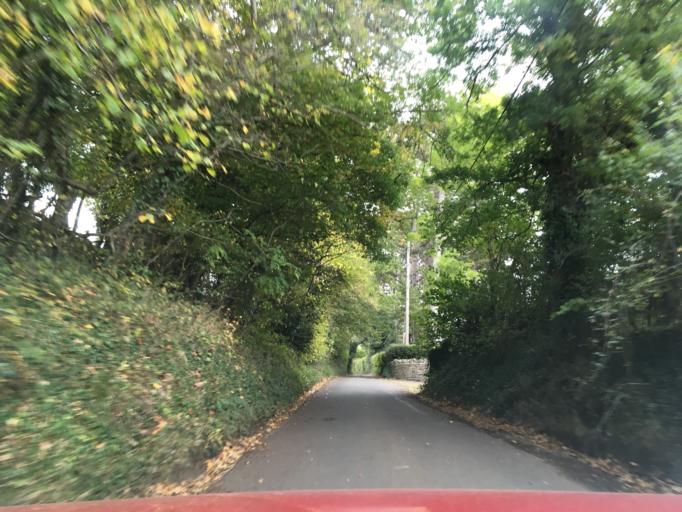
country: GB
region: England
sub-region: South Gloucestershire
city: Wickwar
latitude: 51.5977
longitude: -2.3927
